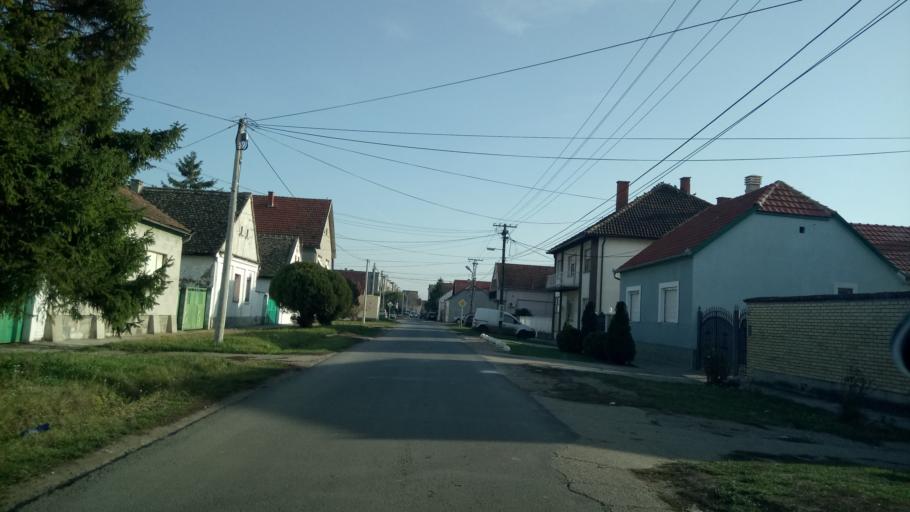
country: RS
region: Autonomna Pokrajina Vojvodina
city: Nova Pazova
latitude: 44.9486
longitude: 20.2192
